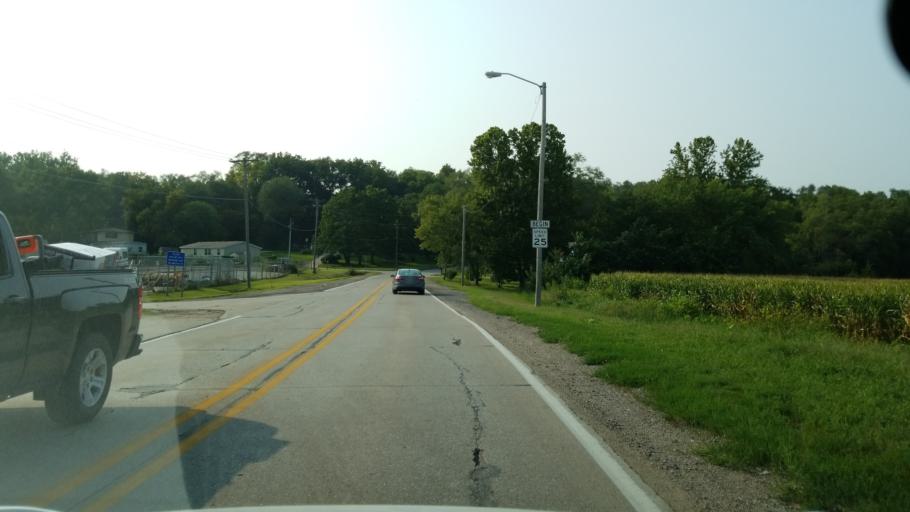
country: US
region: Nebraska
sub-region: Sarpy County
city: Bellevue
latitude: 41.1274
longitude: -95.8909
